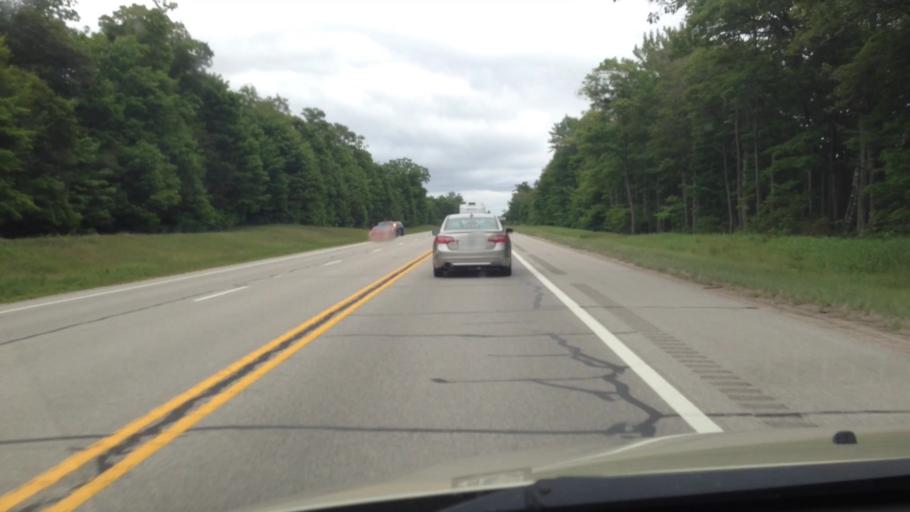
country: US
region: Michigan
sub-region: Mackinac County
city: Saint Ignace
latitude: 46.0250
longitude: -85.0610
